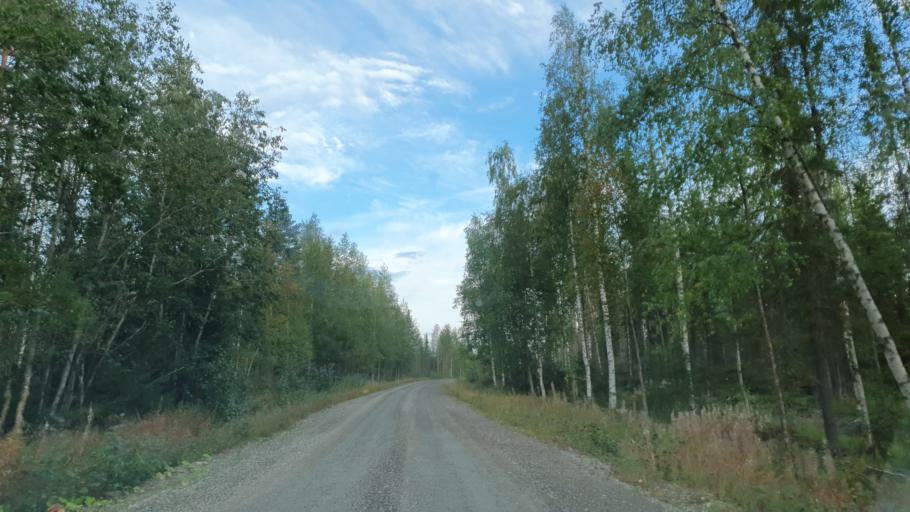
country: FI
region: Kainuu
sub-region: Kehys-Kainuu
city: Kuhmo
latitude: 64.3685
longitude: 29.5670
